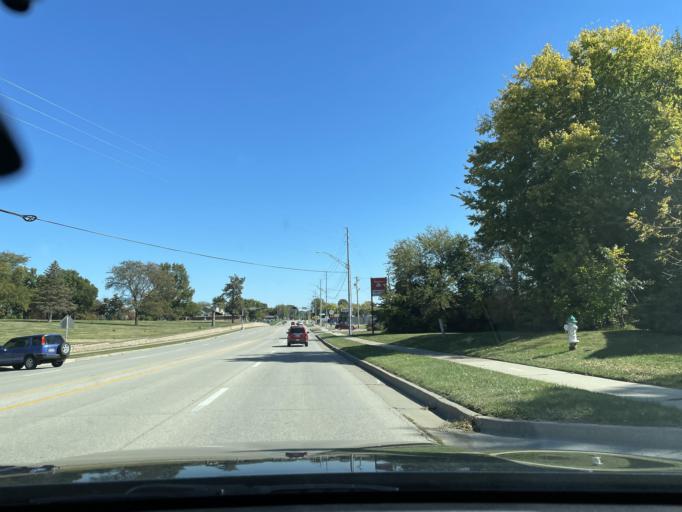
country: US
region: Missouri
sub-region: Buchanan County
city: Saint Joseph
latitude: 39.7793
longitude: -94.7827
